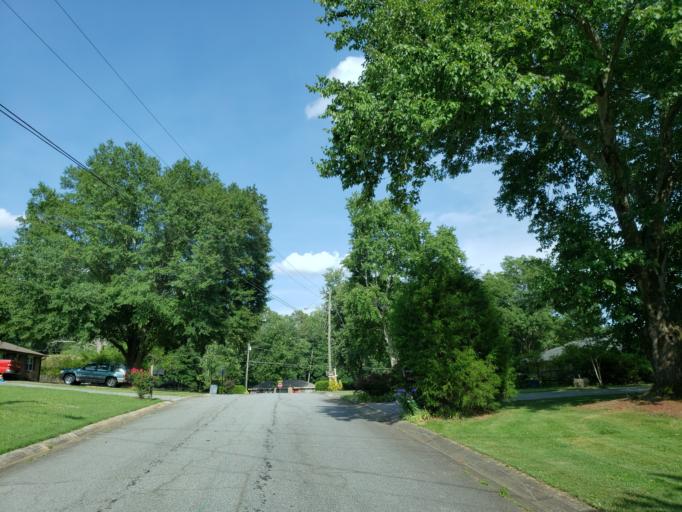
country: US
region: Georgia
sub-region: Cobb County
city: Austell
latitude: 33.8742
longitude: -84.6191
